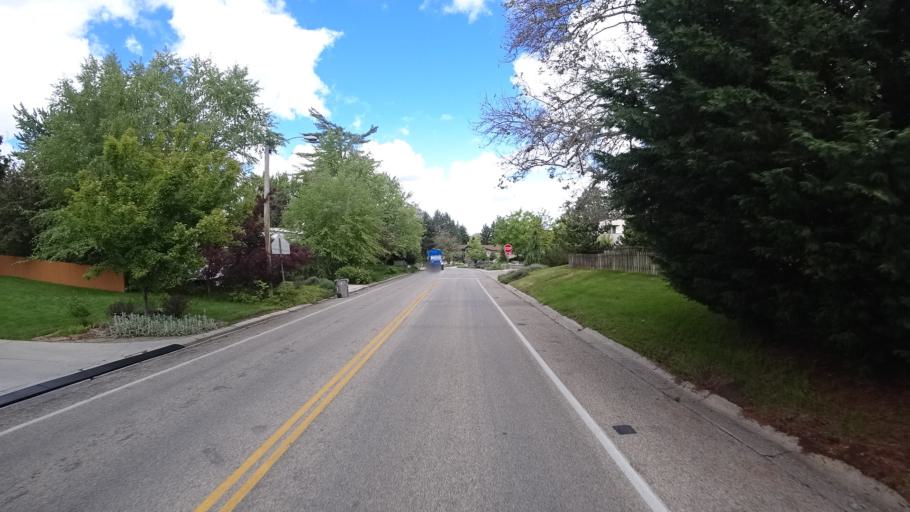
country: US
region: Idaho
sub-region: Ada County
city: Boise
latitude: 43.6458
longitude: -116.1971
